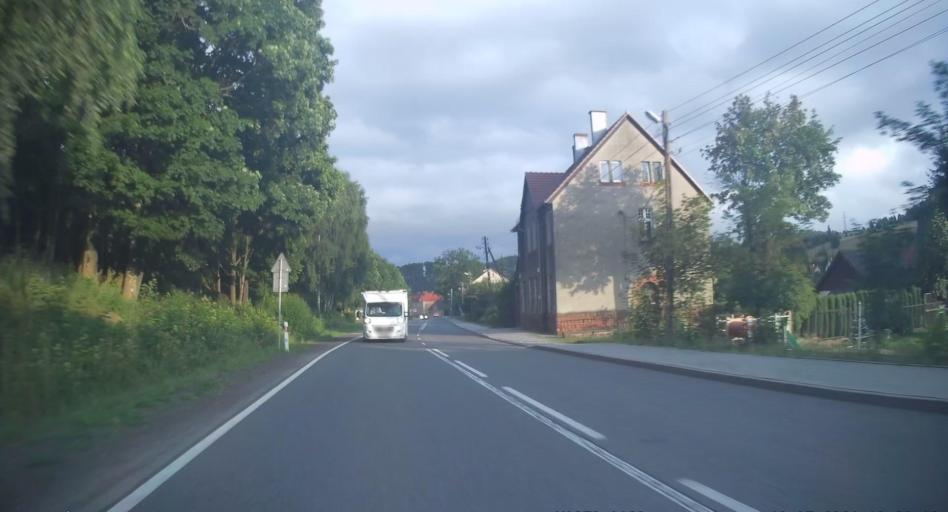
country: PL
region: Lower Silesian Voivodeship
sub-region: Powiat klodzki
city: Ludwikowice Klodzkie
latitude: 50.6195
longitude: 16.4761
